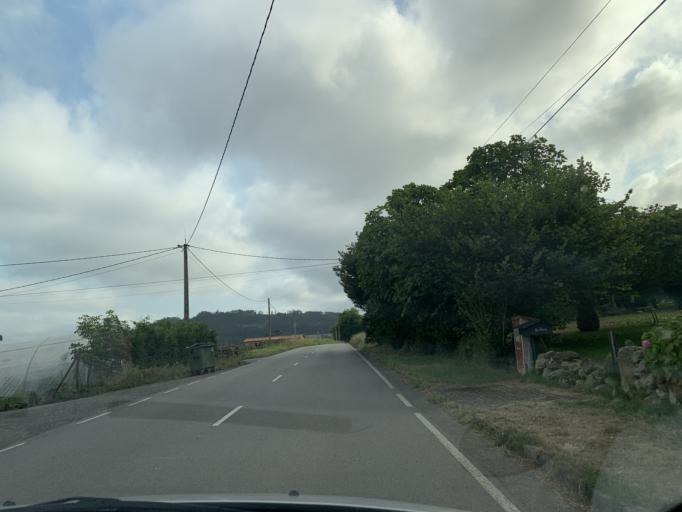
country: ES
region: Asturias
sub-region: Province of Asturias
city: Villaviciosa
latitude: 43.5307
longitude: -5.4300
